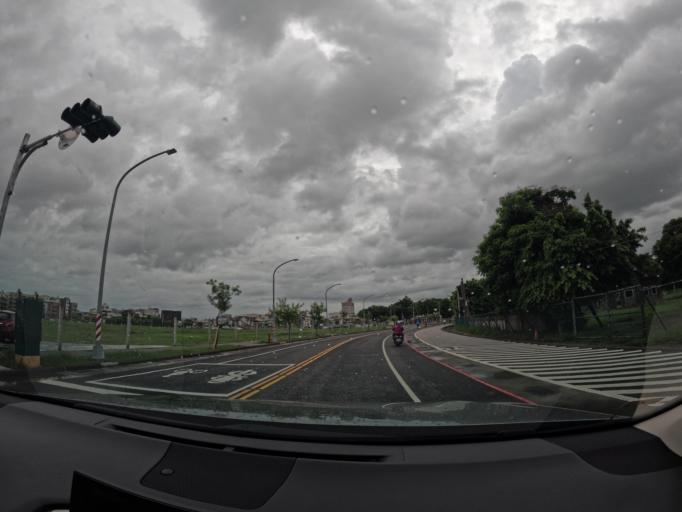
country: TW
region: Taiwan
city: Fengshan
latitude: 22.6323
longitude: 120.3734
